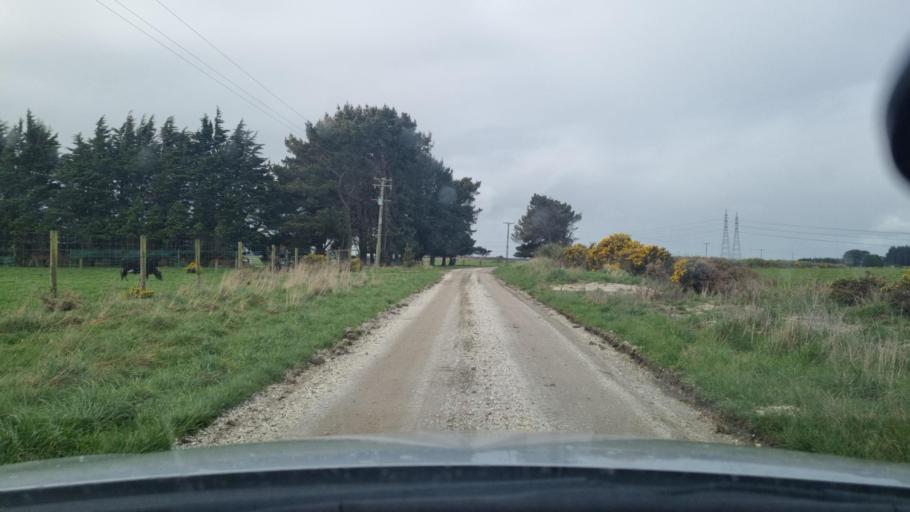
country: NZ
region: Southland
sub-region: Invercargill City
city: Invercargill
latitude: -46.4925
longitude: 168.4272
